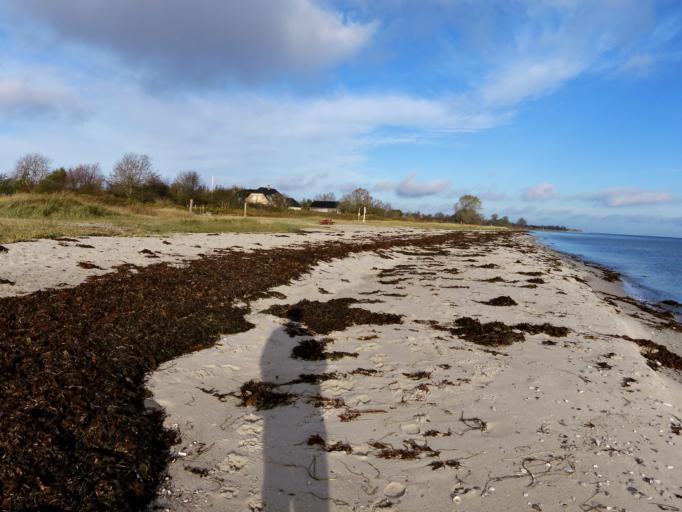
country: DK
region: Central Jutland
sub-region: Odder Kommune
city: Odder
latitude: 55.9251
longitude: 10.2578
